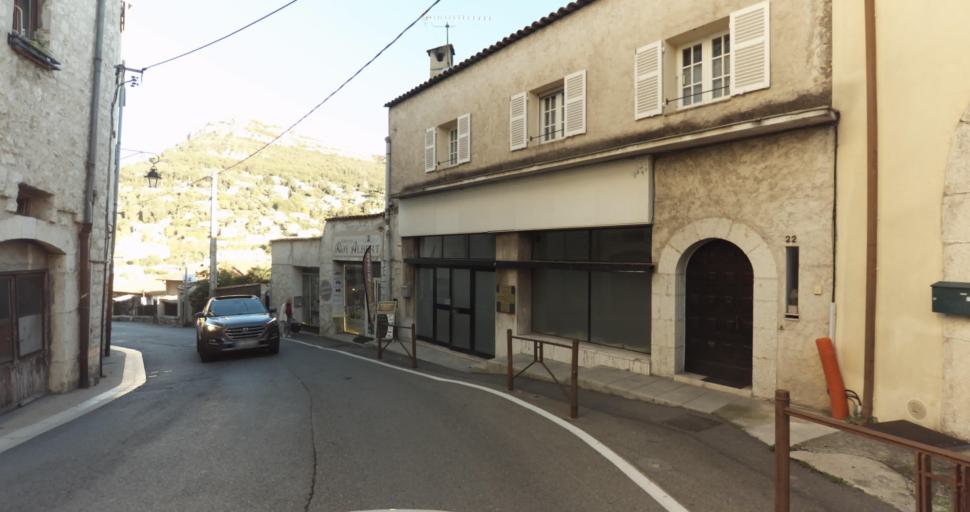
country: FR
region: Provence-Alpes-Cote d'Azur
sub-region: Departement des Alpes-Maritimes
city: Vence
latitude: 43.7227
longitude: 7.1151
